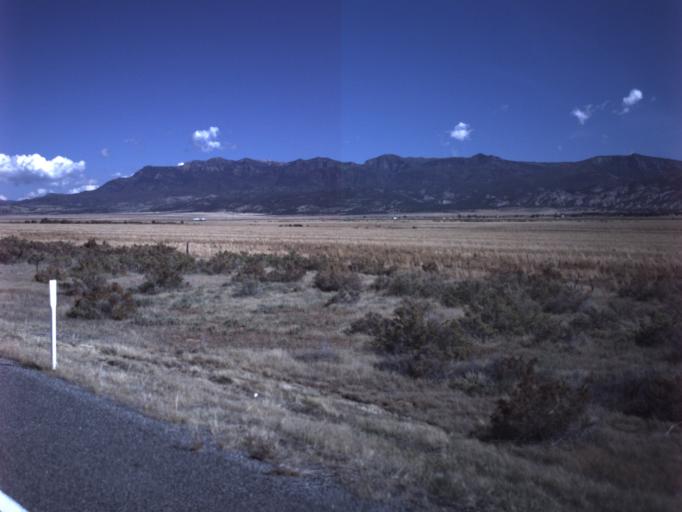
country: US
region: Utah
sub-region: Juab County
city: Nephi
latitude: 39.5484
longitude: -111.9244
